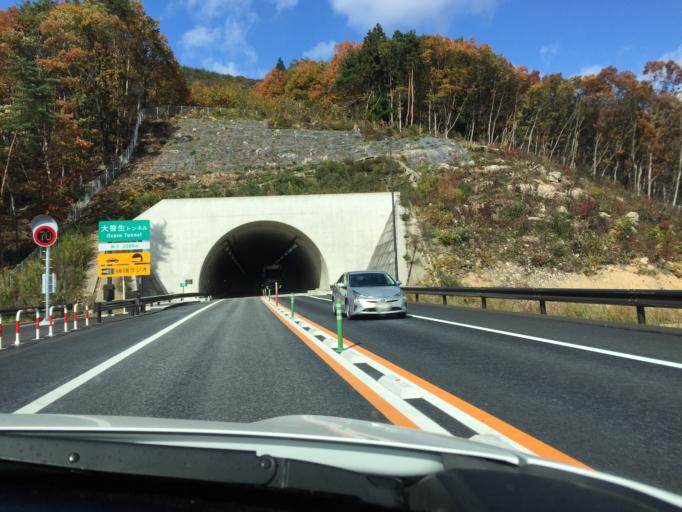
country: JP
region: Fukushima
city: Fukushima-shi
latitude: 37.8086
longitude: 140.4068
